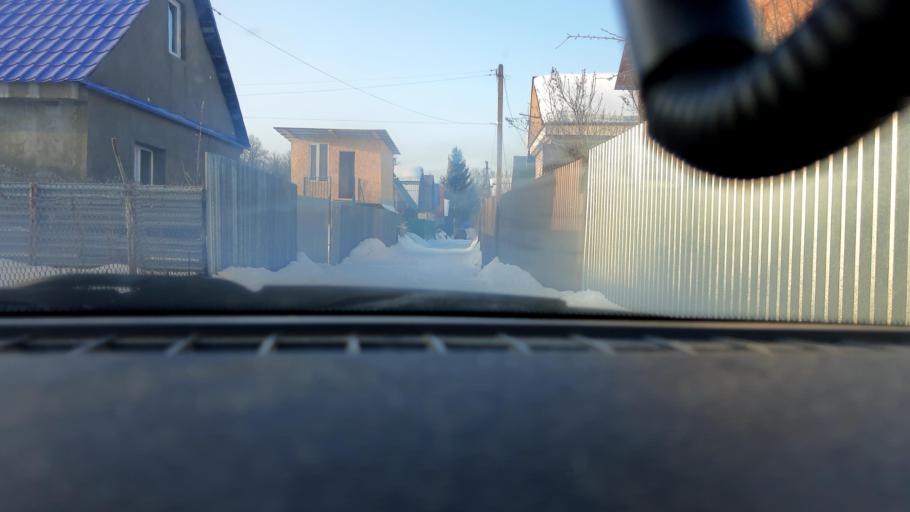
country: RU
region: Bashkortostan
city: Ufa
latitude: 54.6856
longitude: 55.8879
